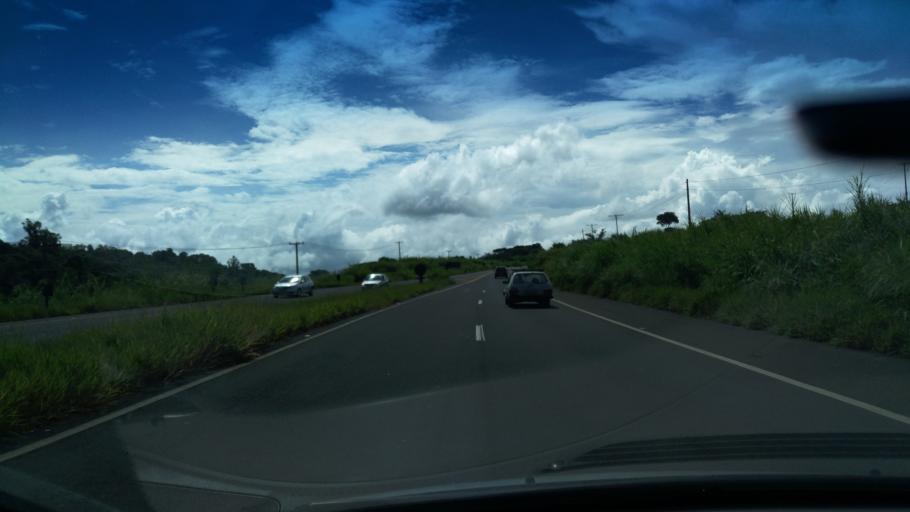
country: BR
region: Sao Paulo
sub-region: Santo Antonio Do Jardim
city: Espirito Santo do Pinhal
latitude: -22.1642
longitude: -46.7359
